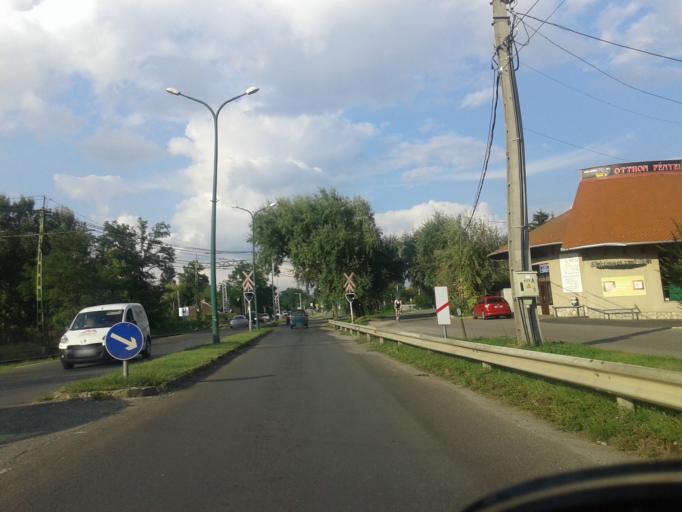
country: HU
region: Pest
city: Dunaharaszti
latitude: 47.3643
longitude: 19.0903
